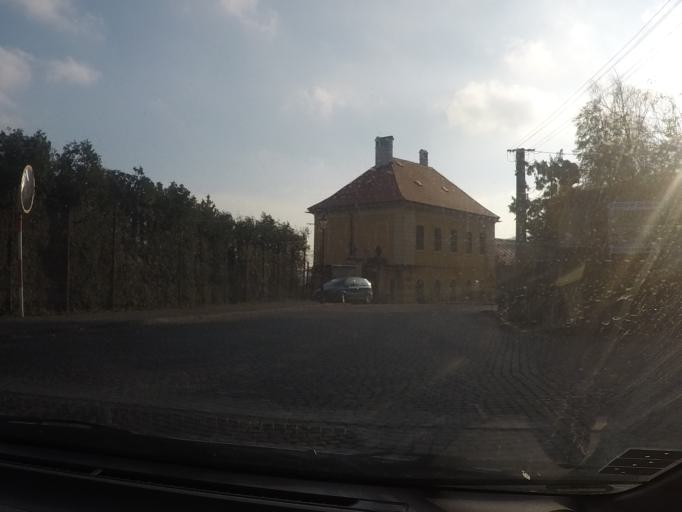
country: SK
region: Banskobystricky
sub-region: Okres Banska Bystrica
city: Banska Stiavnica
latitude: 48.4611
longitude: 18.9010
